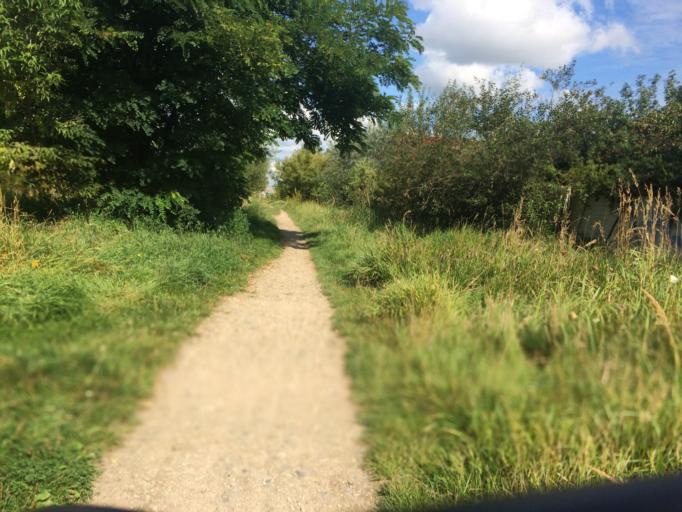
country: DE
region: Berlin
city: Heinersdorf
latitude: 52.5669
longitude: 13.4468
